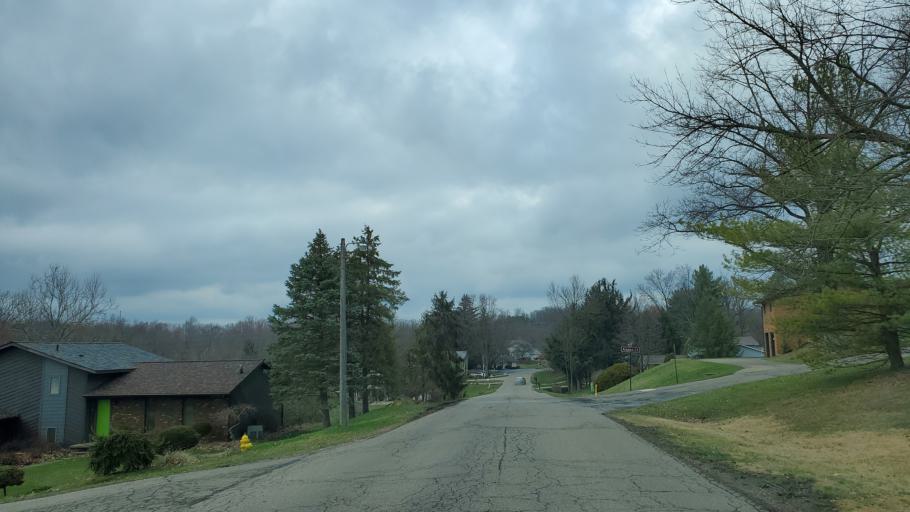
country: US
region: Ohio
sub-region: Licking County
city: Newark
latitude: 40.0284
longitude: -82.3804
